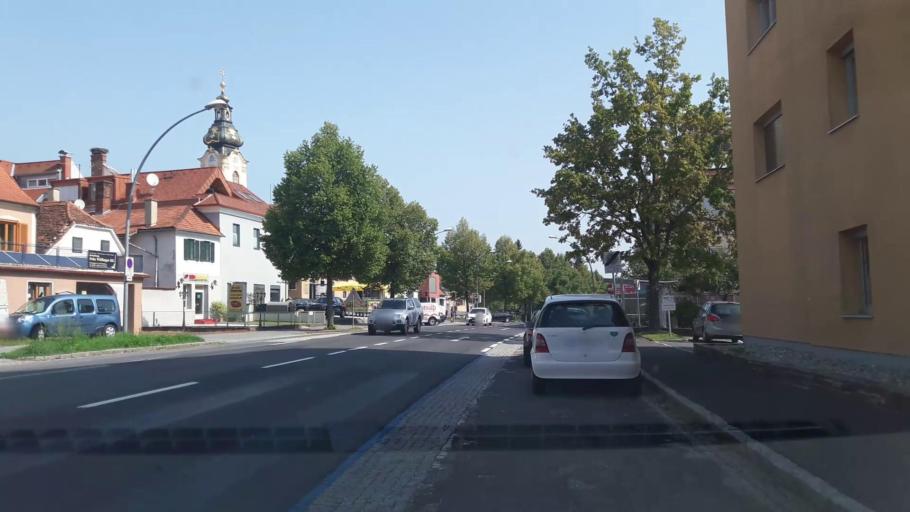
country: AT
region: Styria
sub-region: Politischer Bezirk Hartberg-Fuerstenfeld
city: Hartberg
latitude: 47.2789
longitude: 15.9688
